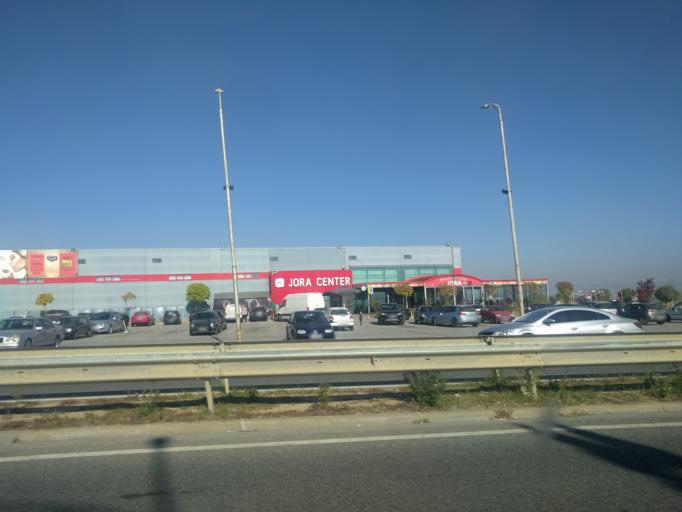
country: XK
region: Pristina
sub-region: Komuna e Drenasit
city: Glogovac
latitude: 42.5763
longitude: 20.8881
